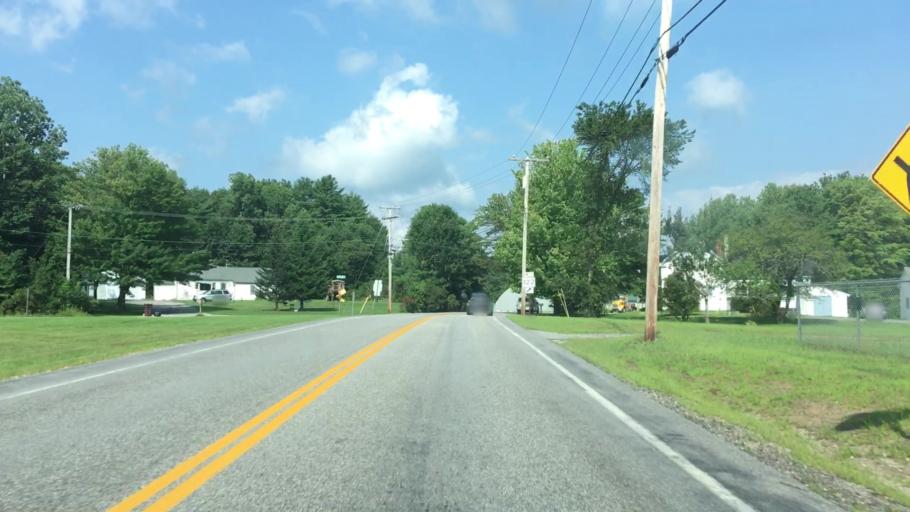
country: US
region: Maine
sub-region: Cumberland County
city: New Gloucester
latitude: 44.0257
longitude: -70.2851
